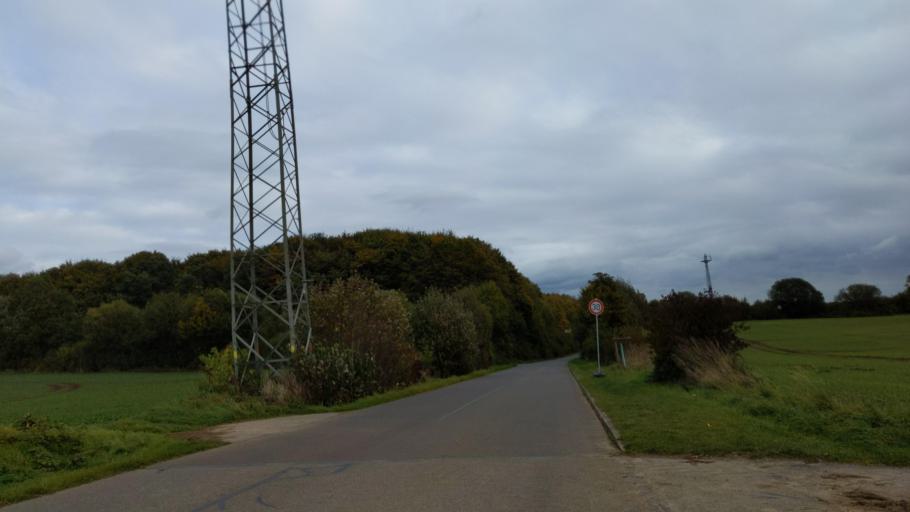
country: DE
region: Schleswig-Holstein
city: Sierksdorf
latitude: 54.0677
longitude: 10.7493
